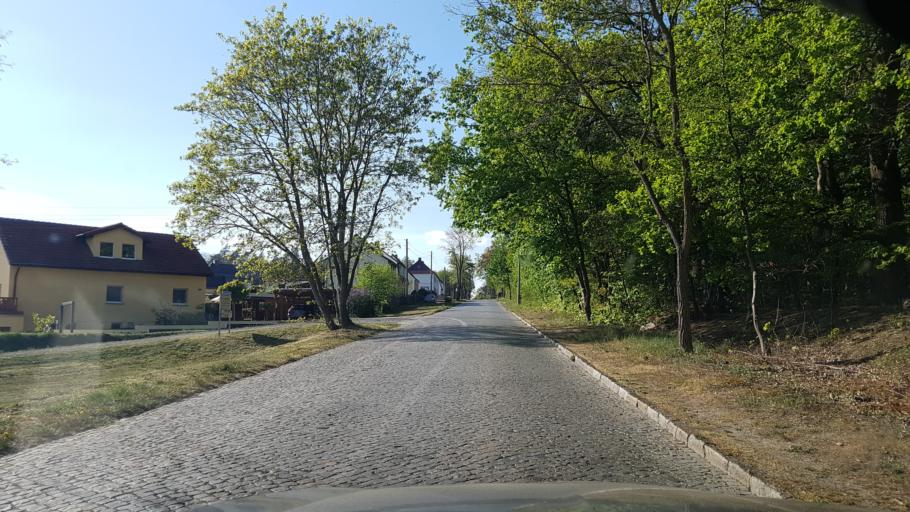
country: DE
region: Brandenburg
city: Elsterwerda
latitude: 51.4766
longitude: 13.5086
